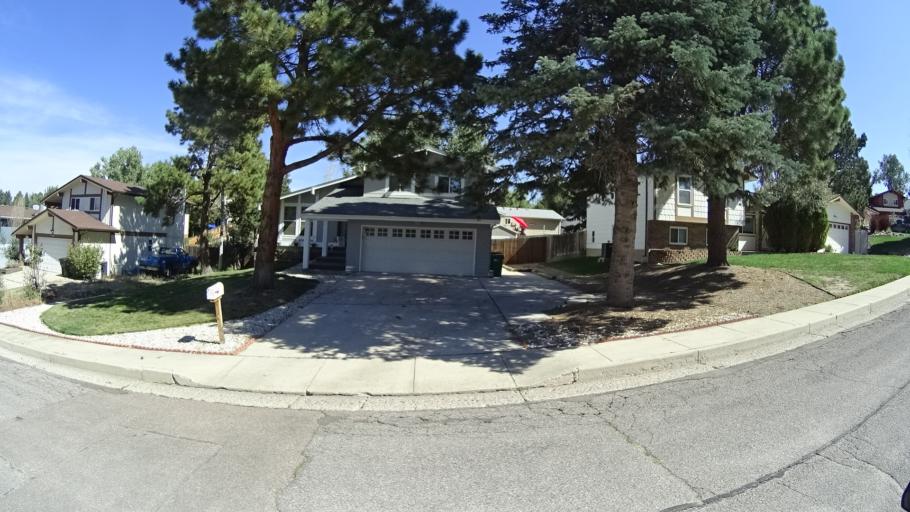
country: US
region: Colorado
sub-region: El Paso County
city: Cimarron Hills
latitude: 38.9133
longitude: -104.7679
